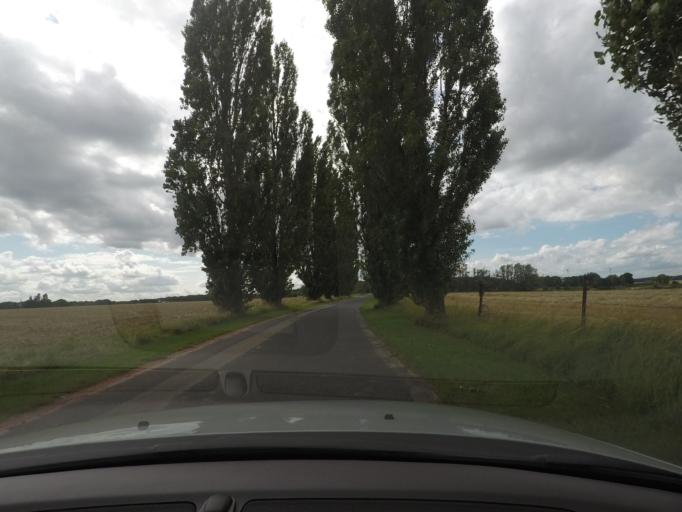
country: FR
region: Haute-Normandie
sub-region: Departement de l'Eure
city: Les Andelys
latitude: 49.2375
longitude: 1.4213
